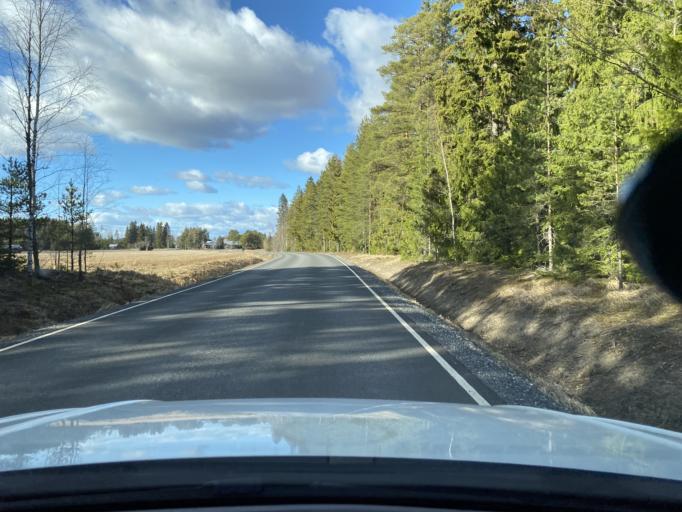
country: FI
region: Pirkanmaa
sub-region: Lounais-Pirkanmaa
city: Punkalaidun
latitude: 61.0929
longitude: 23.2058
